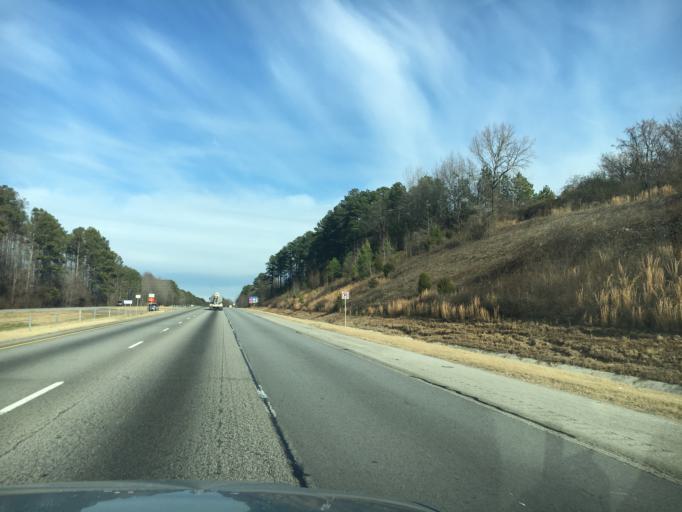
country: US
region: Georgia
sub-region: Franklin County
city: Lavonia
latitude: 34.4325
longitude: -83.1487
